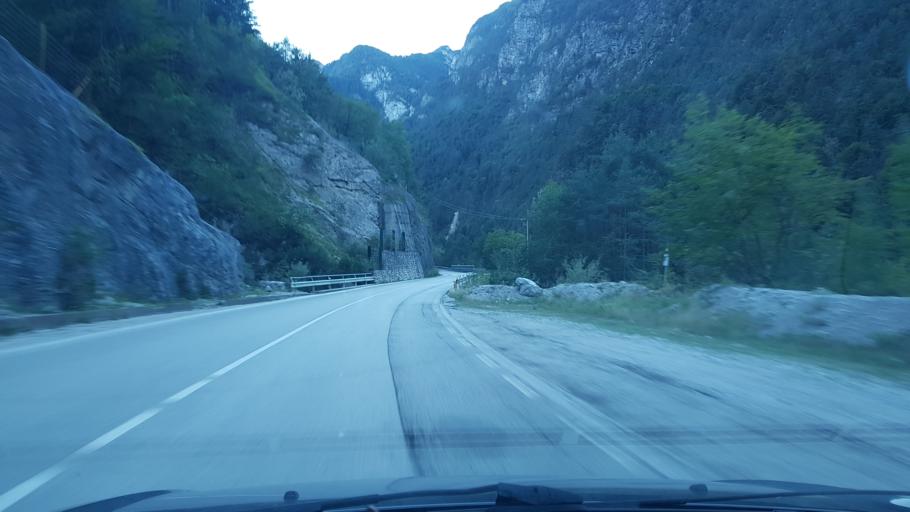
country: IT
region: Veneto
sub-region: Provincia di Belluno
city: Forno di Zoldo
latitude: 46.3196
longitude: 12.2335
